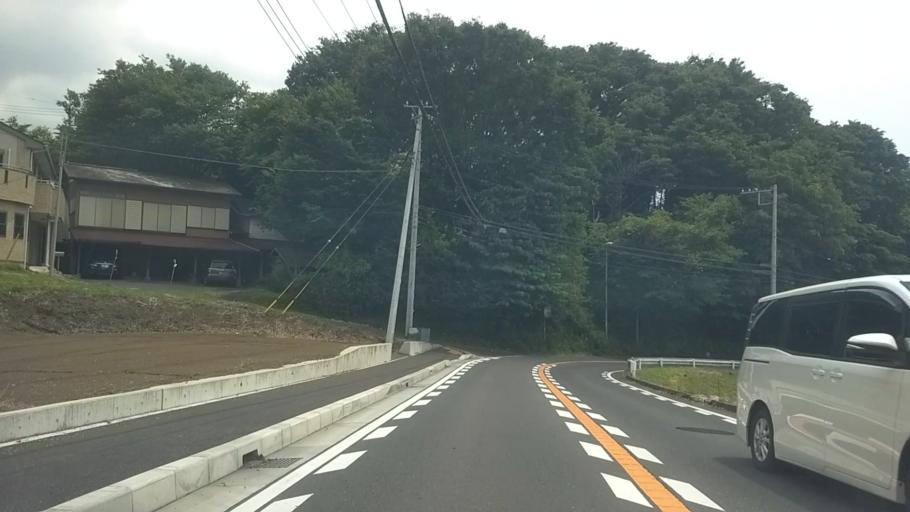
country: JP
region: Kanagawa
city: Chigasaki
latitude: 35.3683
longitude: 139.4219
